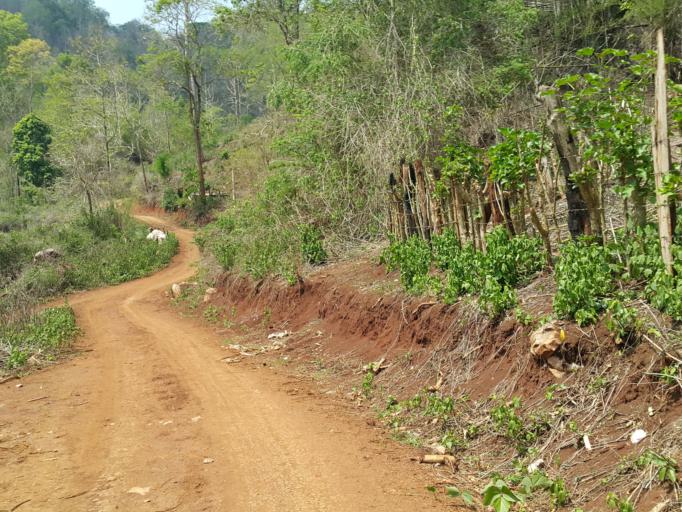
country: TH
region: Chiang Mai
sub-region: Amphoe Chiang Dao
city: Chiang Dao
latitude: 19.3142
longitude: 98.7255
